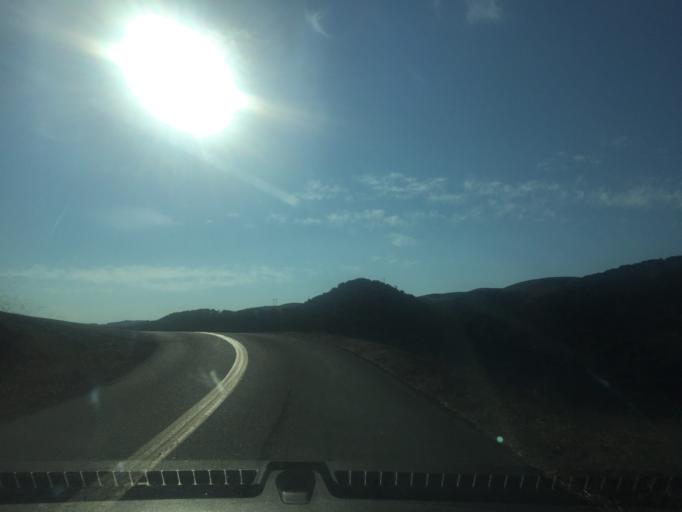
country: US
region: California
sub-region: Santa Barbara County
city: Lompoc
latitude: 34.5148
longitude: -120.4589
